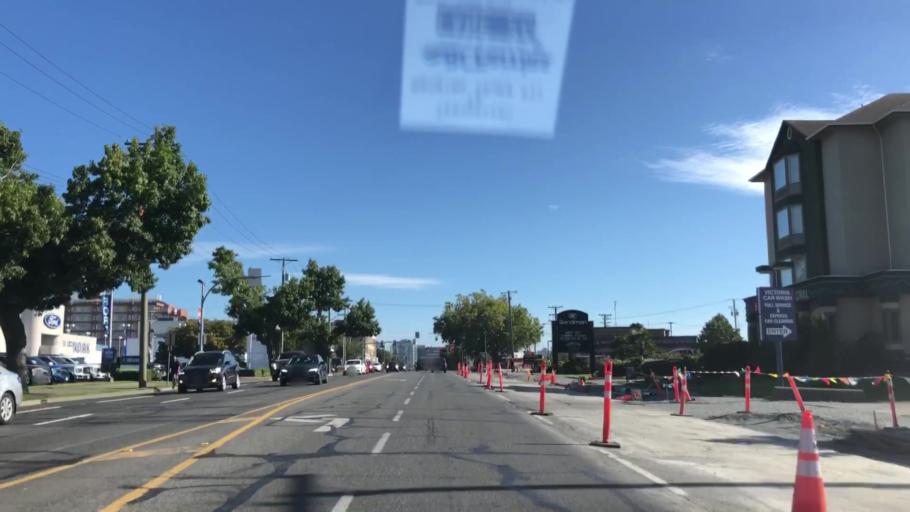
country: CA
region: British Columbia
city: Victoria
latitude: 48.4402
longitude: -123.3680
